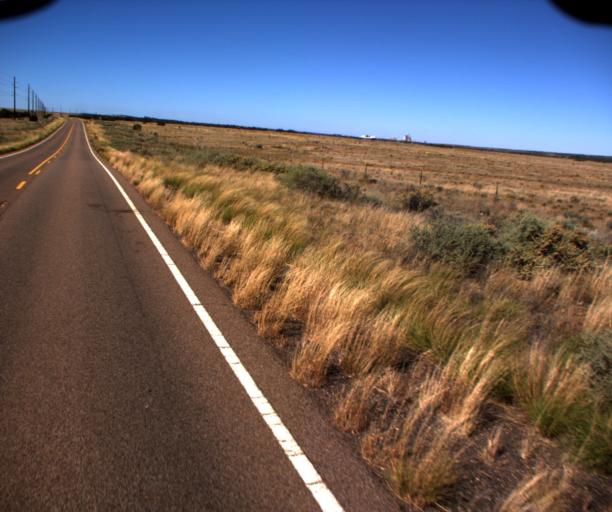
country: US
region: Arizona
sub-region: Navajo County
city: Taylor
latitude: 34.4830
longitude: -110.2844
